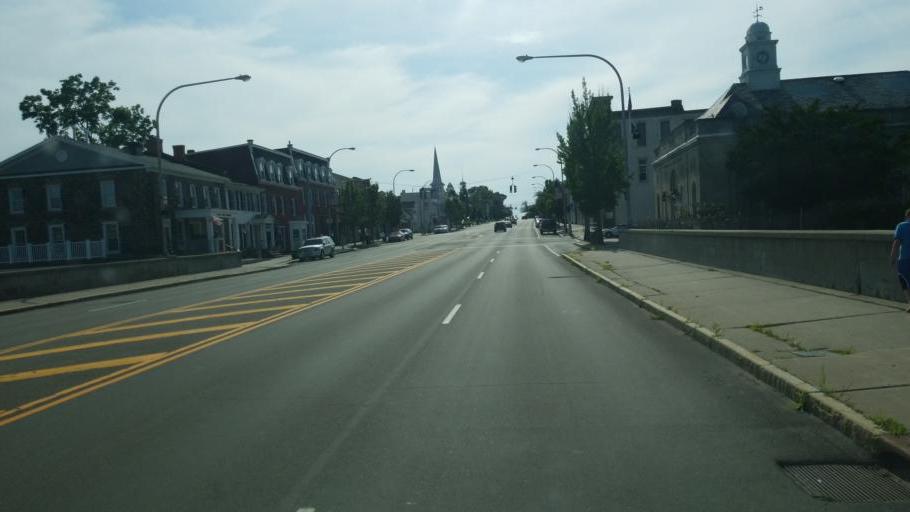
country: US
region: New York
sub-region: Genesee County
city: Le Roy
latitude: 42.9777
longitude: -77.9884
